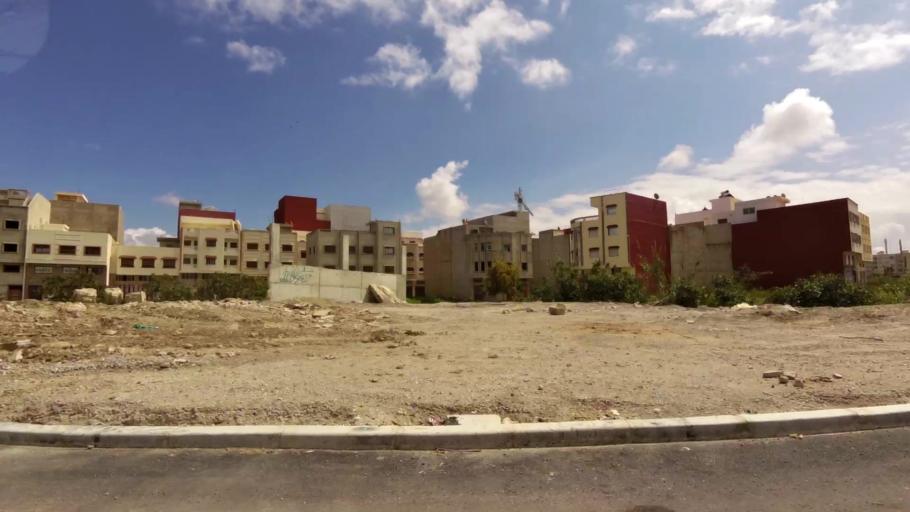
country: MA
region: Tanger-Tetouan
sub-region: Tanger-Assilah
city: Tangier
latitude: 35.7632
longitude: -5.8460
